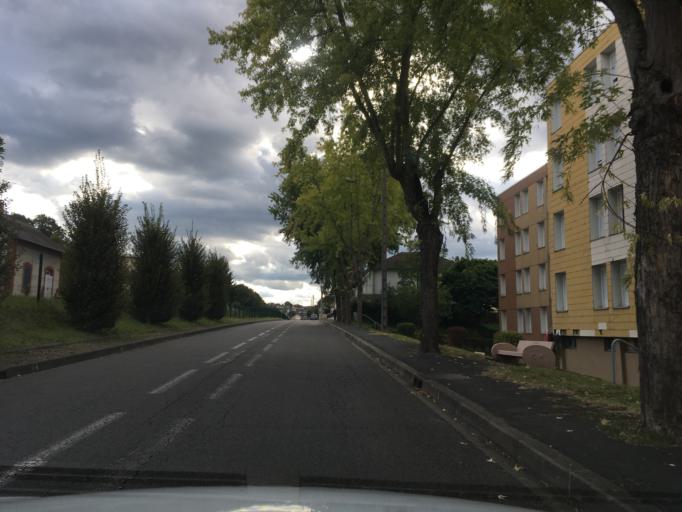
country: FR
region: Limousin
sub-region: Departement de la Correze
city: Brive-la-Gaillarde
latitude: 45.1533
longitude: 1.5491
